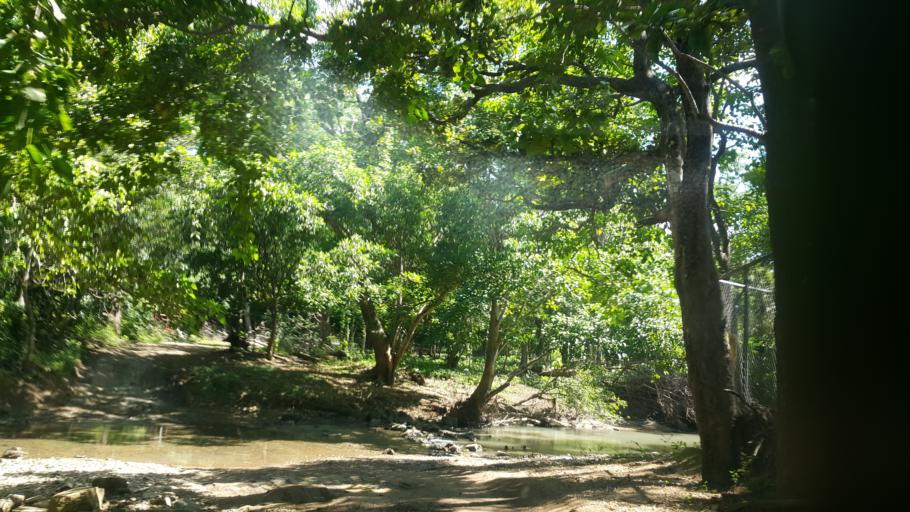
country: NI
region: Rivas
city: San Juan del Sur
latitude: 11.2880
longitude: -85.8998
